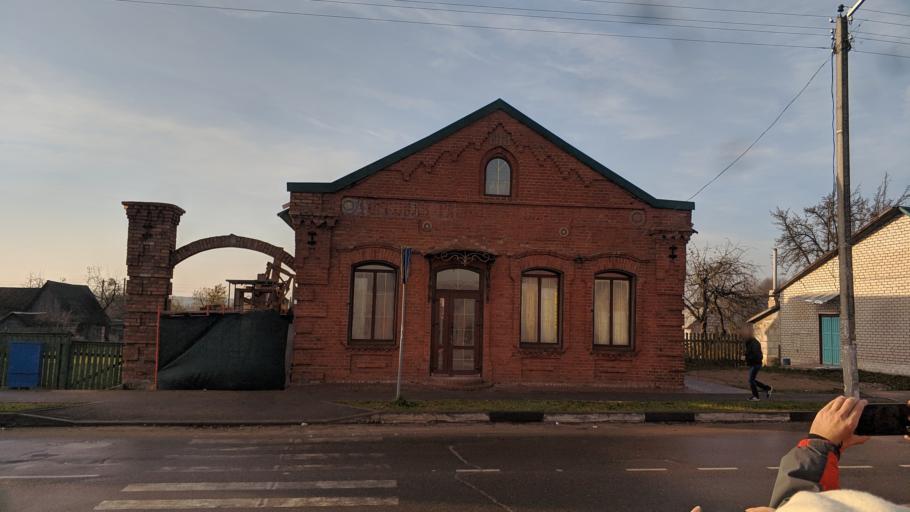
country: BY
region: Minsk
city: Uzda
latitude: 53.4573
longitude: 27.2193
